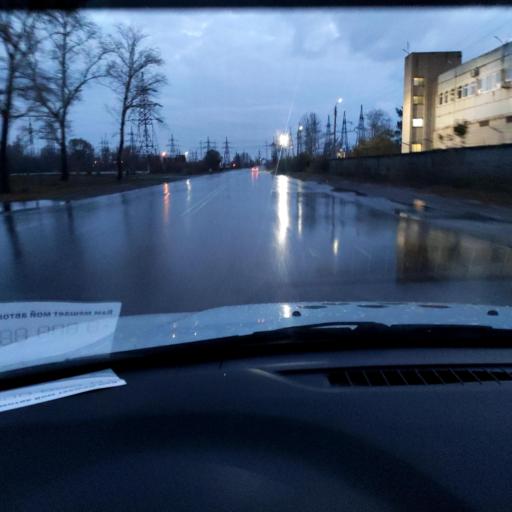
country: RU
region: Samara
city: Zhigulevsk
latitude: 53.5128
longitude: 49.4633
